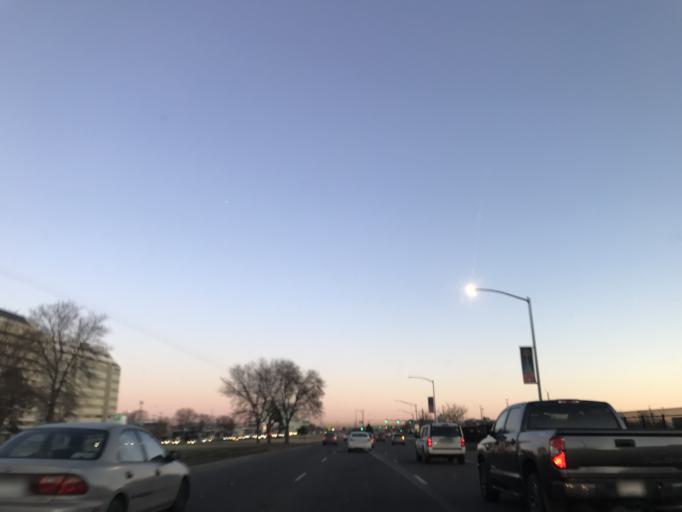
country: US
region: Colorado
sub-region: Adams County
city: Commerce City
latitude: 39.7630
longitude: -104.9028
